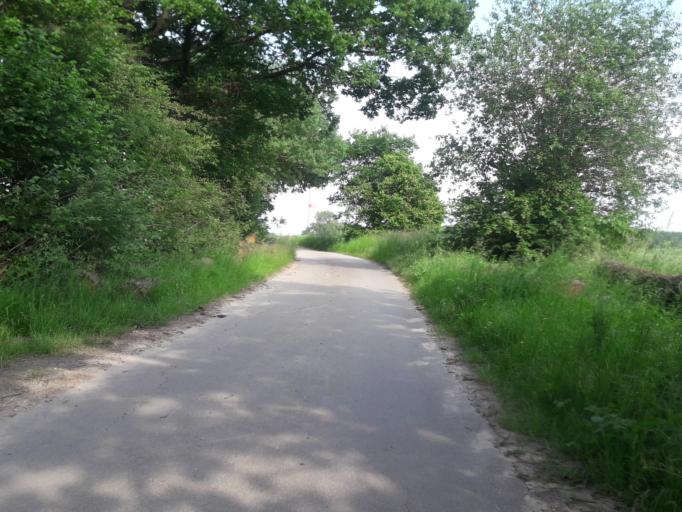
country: DE
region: North Rhine-Westphalia
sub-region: Regierungsbezirk Detmold
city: Salzkotten
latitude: 51.7017
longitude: 8.6470
